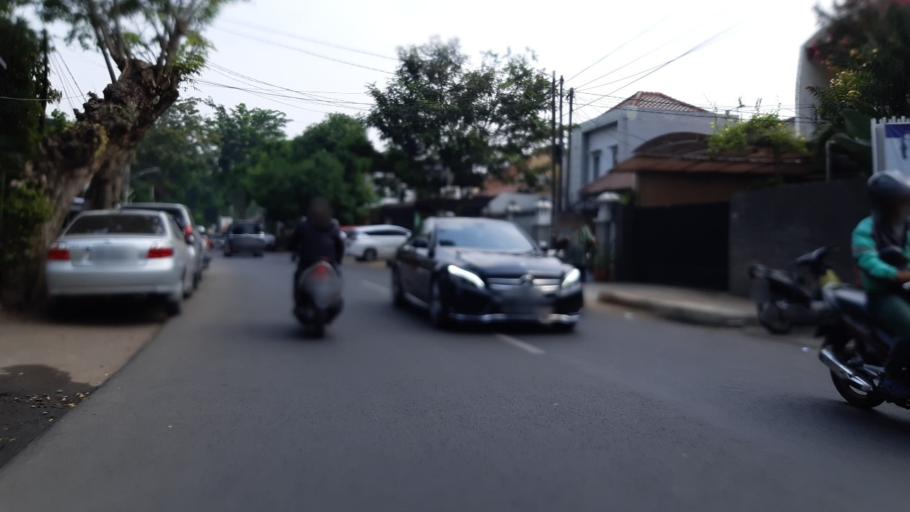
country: ID
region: Jakarta Raya
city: Jakarta
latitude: -6.2319
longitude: 106.8550
